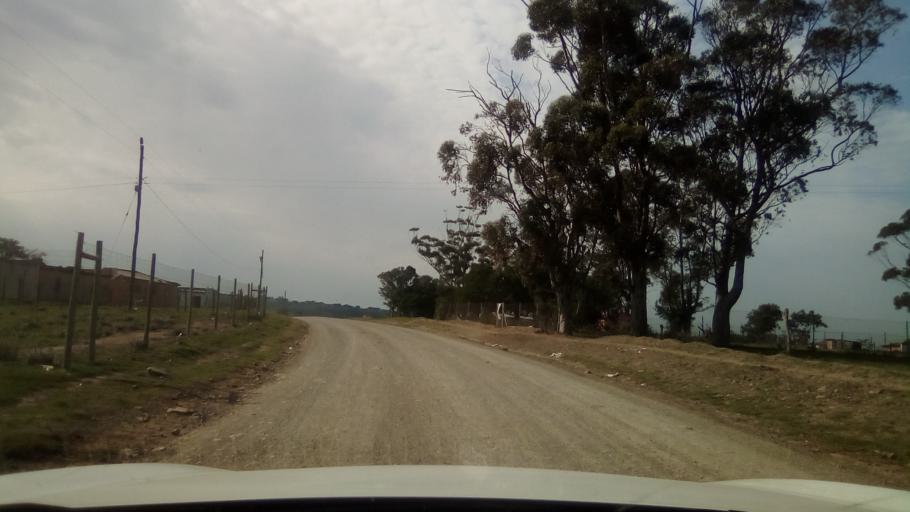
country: ZA
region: Eastern Cape
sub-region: Buffalo City Metropolitan Municipality
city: Bhisho
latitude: -32.9859
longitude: 27.2729
